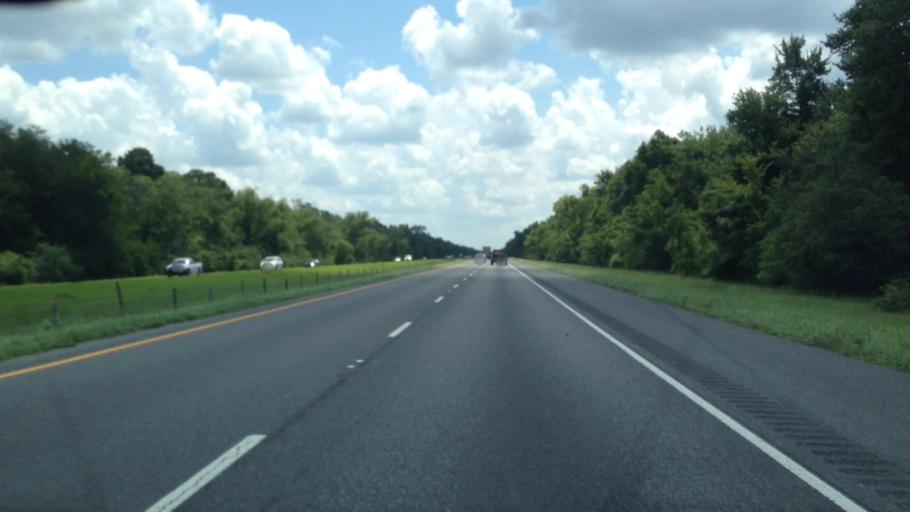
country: US
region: Louisiana
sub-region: Saint James Parish
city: Grand Point
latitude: 30.1389
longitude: -90.7441
